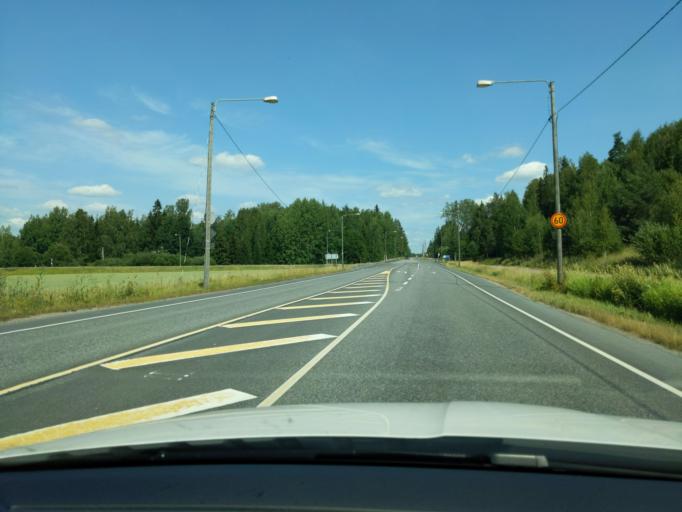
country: FI
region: Uusimaa
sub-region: Helsinki
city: Kerava
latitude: 60.3586
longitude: 25.1277
